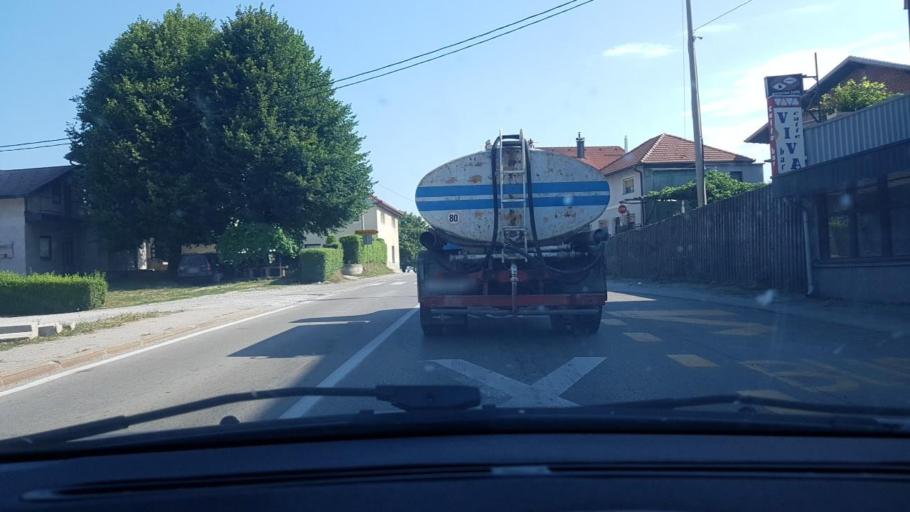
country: BA
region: Federation of Bosnia and Herzegovina
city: Skokovi
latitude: 45.0307
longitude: 15.9141
